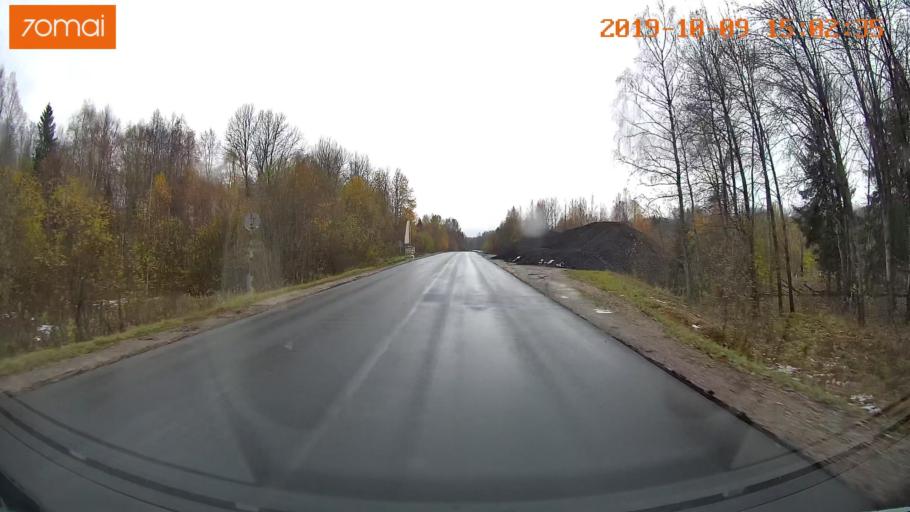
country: RU
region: Kostroma
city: Chistyye Bory
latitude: 58.2830
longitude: 41.6784
